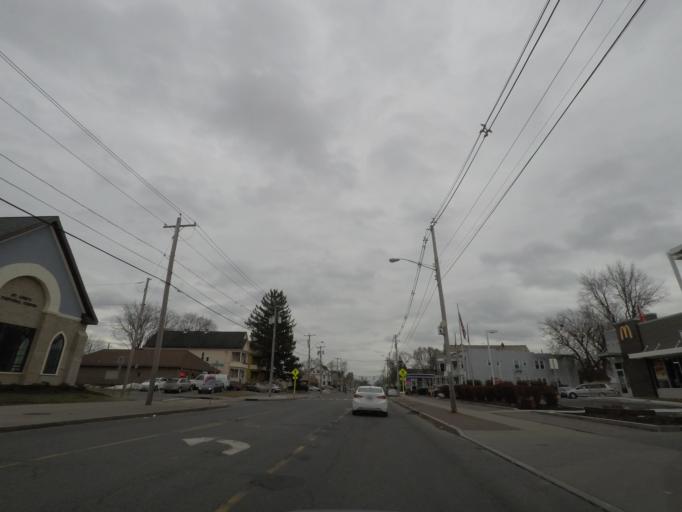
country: US
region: New York
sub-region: Schenectady County
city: Schenectady
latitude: 42.7984
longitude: -73.9244
